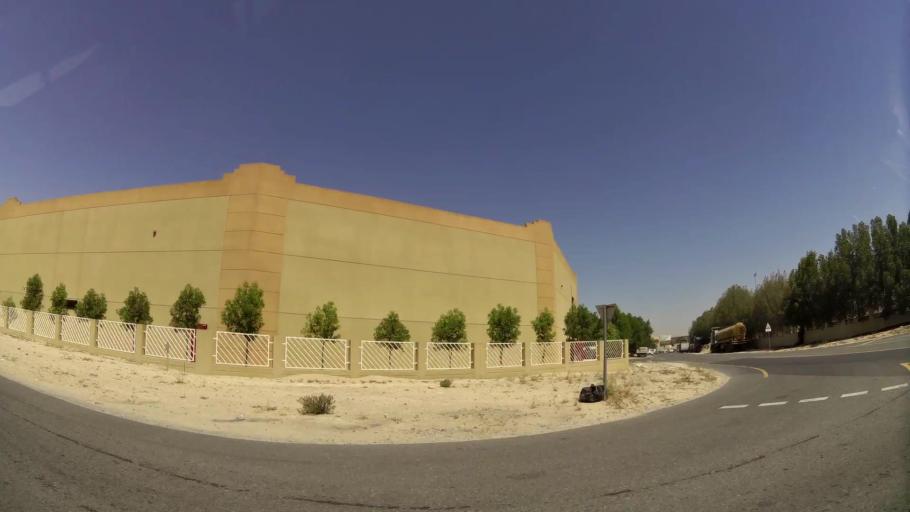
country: AE
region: Dubai
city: Dubai
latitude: 24.9782
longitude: 55.2075
